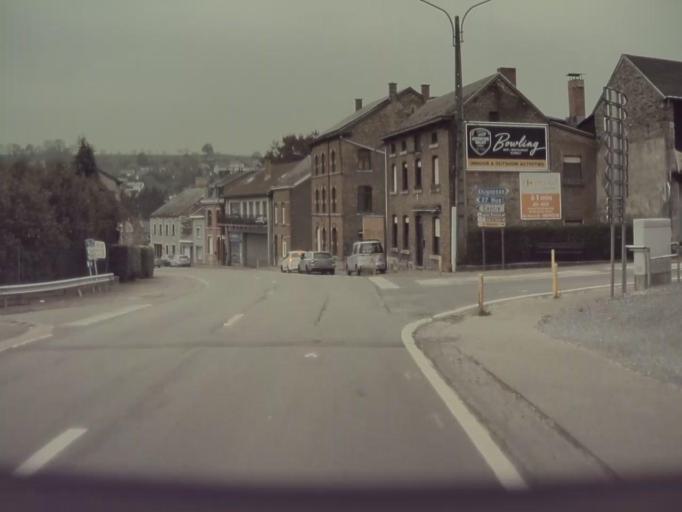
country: BE
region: Wallonia
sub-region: Province de Liege
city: Hamoir
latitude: 50.4246
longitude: 5.5390
